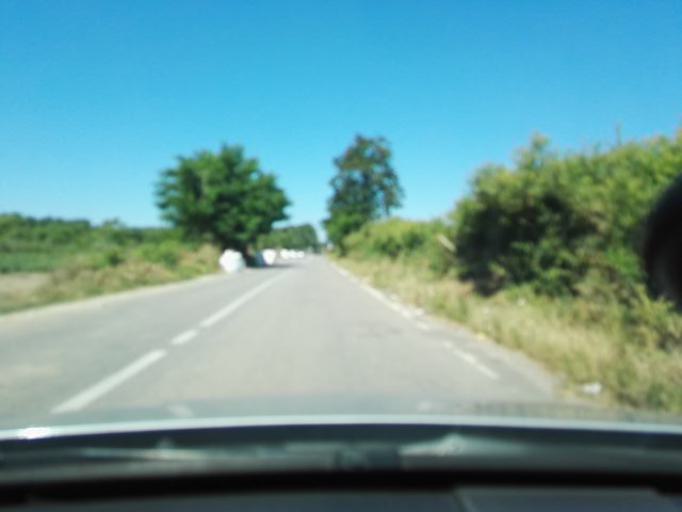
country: IT
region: Campania
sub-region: Provincia di Caserta
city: Villa di Briano
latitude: 40.9855
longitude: 14.1601
